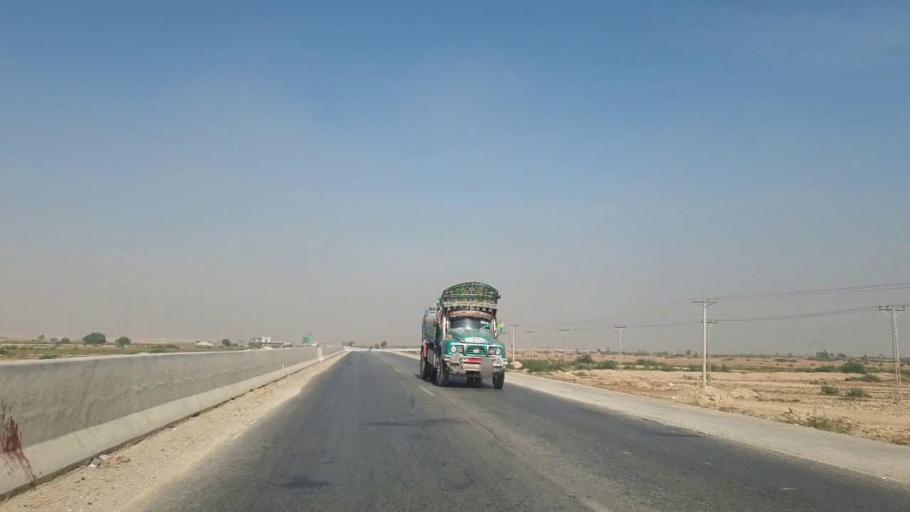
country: PK
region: Sindh
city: Jamshoro
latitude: 25.5176
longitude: 68.2741
